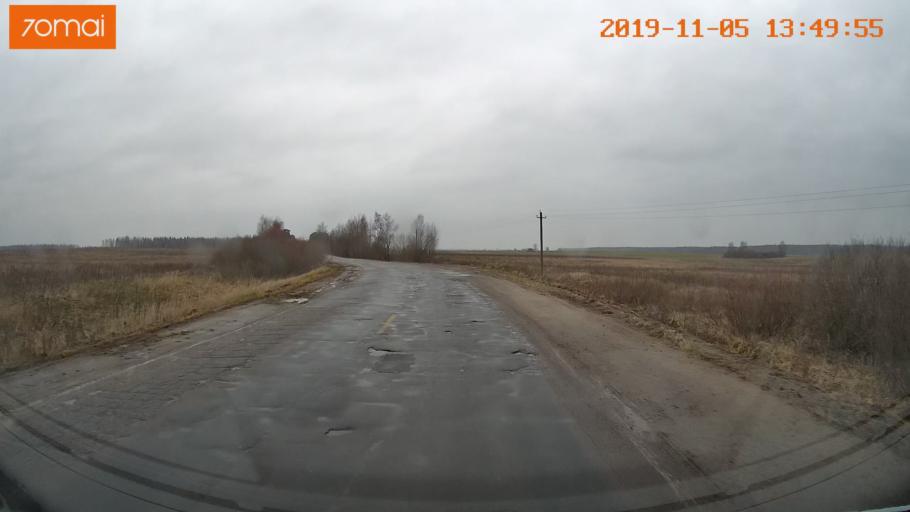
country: RU
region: Ivanovo
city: Kaminskiy
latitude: 57.0152
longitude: 41.4107
